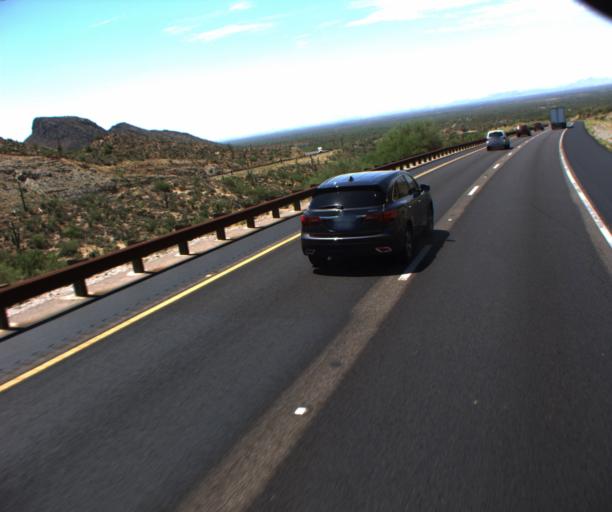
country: US
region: Arizona
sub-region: Pinal County
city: Gold Camp
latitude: 33.2716
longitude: -111.2423
